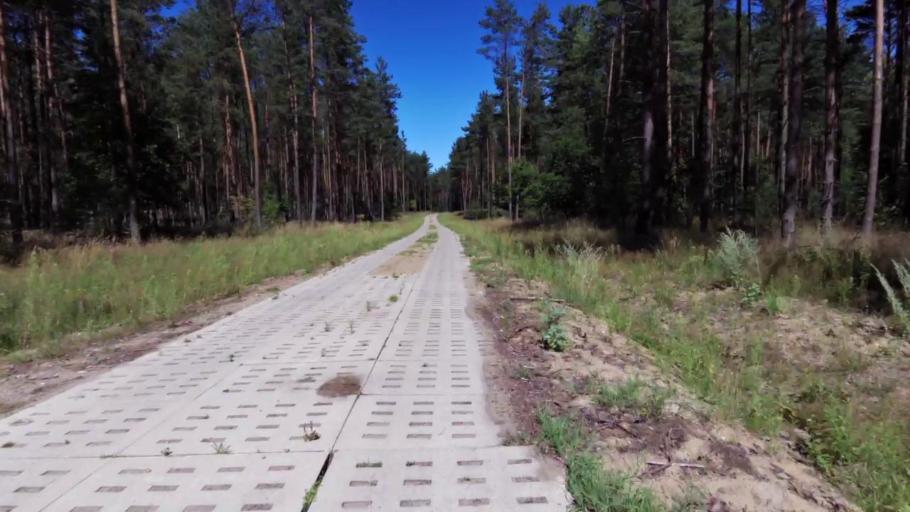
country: PL
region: West Pomeranian Voivodeship
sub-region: Powiat szczecinecki
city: Szczecinek
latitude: 53.6245
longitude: 16.6615
